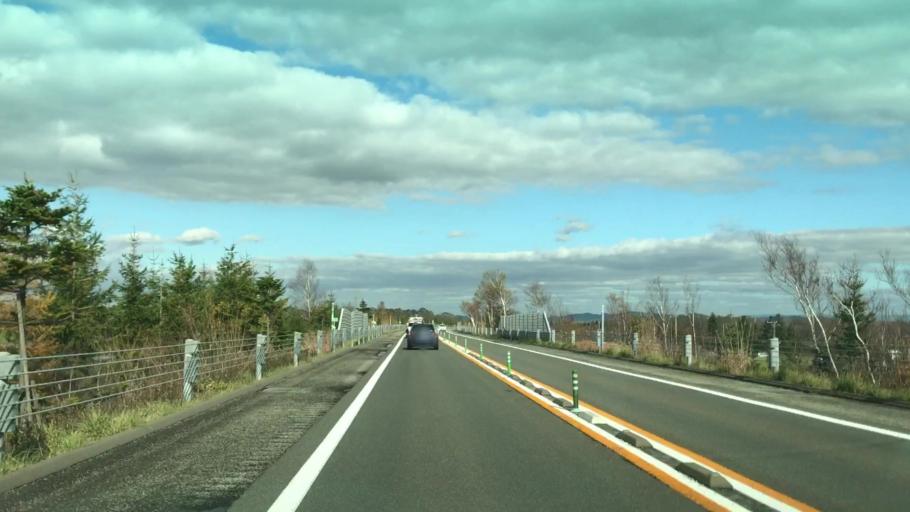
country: JP
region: Hokkaido
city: Chitose
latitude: 42.8783
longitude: 141.6181
